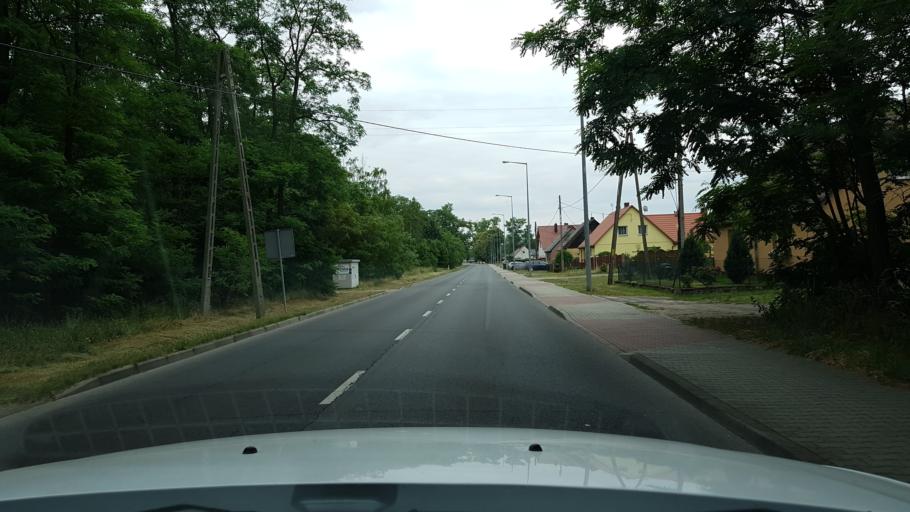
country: PL
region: Lubusz
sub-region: Powiat gorzowski
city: Kostrzyn nad Odra
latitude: 52.6175
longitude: 14.6127
